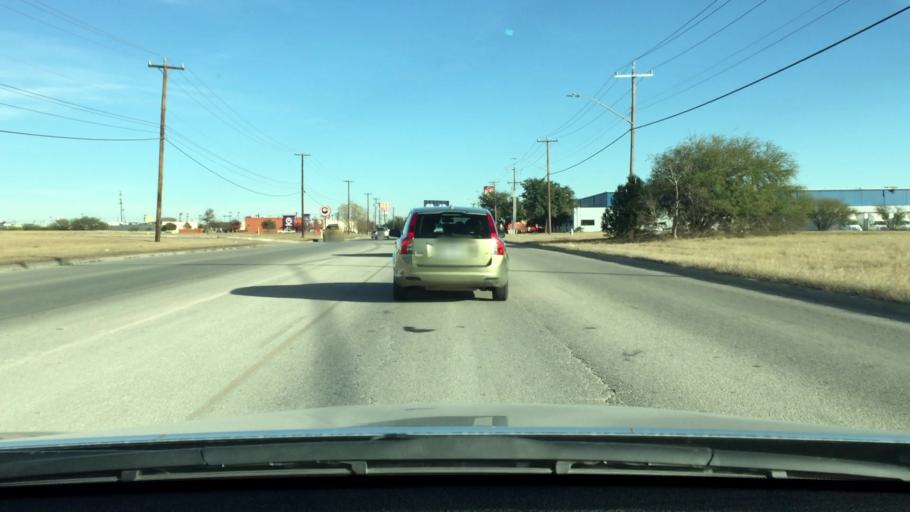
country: US
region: Texas
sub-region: Bexar County
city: Kirby
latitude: 29.4816
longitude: -98.3656
